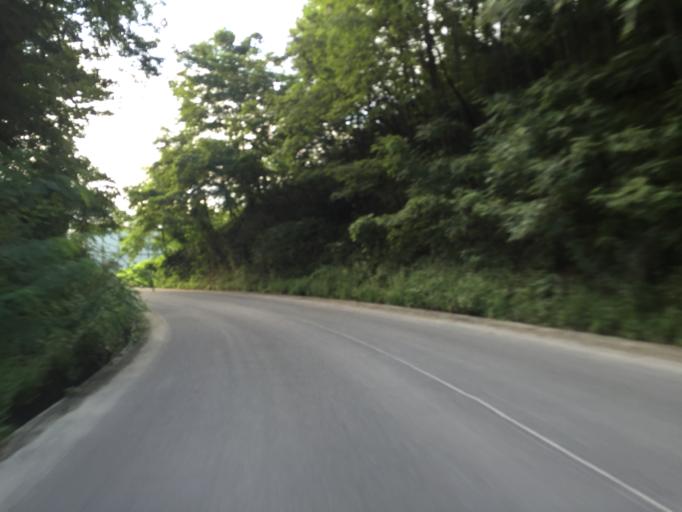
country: JP
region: Fukushima
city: Fukushima-shi
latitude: 37.6563
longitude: 140.5762
